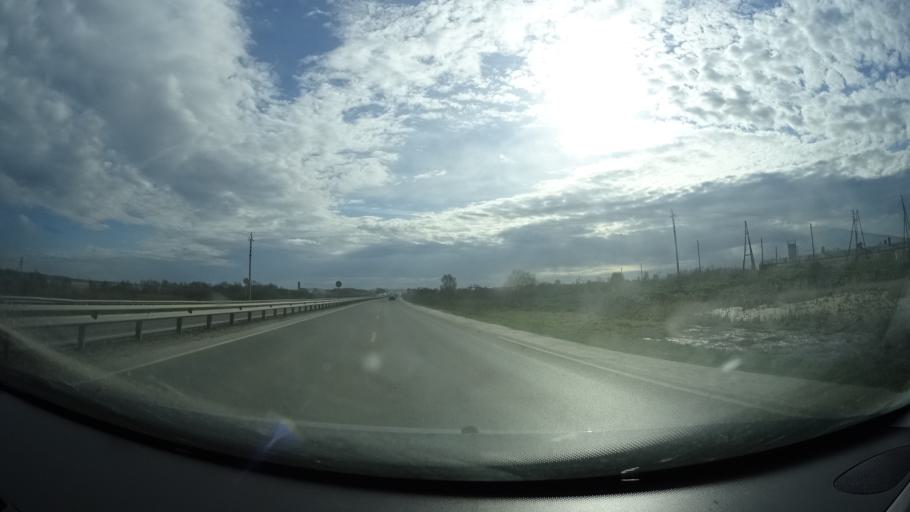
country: RU
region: Perm
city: Kultayevo
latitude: 57.9060
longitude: 55.9862
